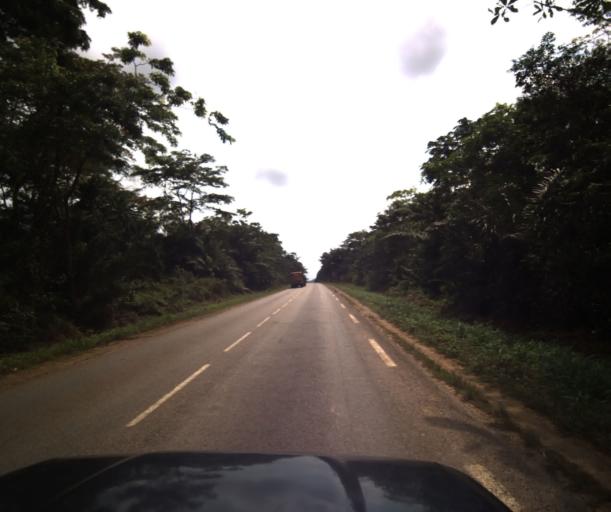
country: CM
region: Centre
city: Eseka
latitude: 3.8499
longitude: 10.5069
